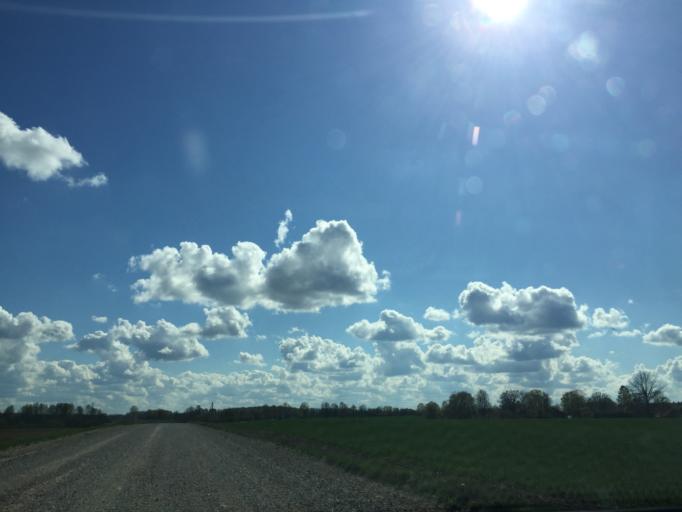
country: LV
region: Strenci
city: Strenci
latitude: 57.4947
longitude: 25.6427
